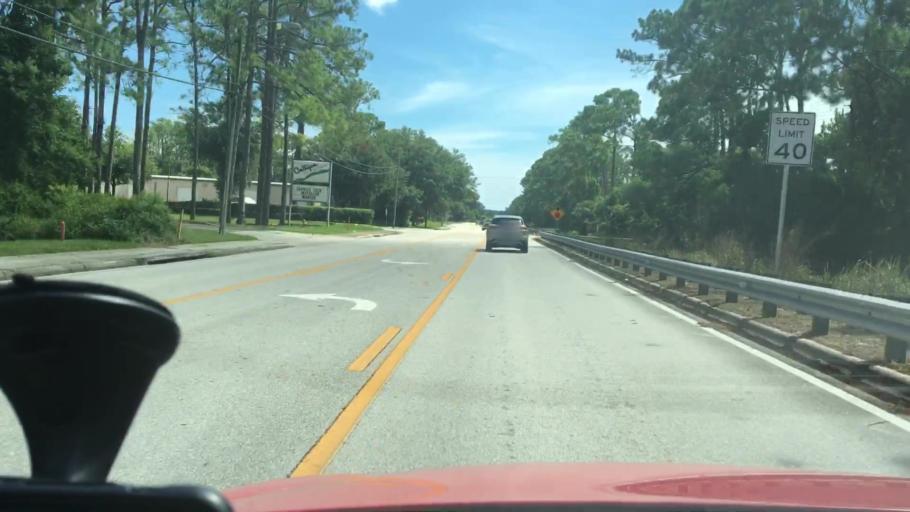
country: US
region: Florida
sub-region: Volusia County
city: Holly Hill
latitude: 29.2023
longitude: -81.0859
